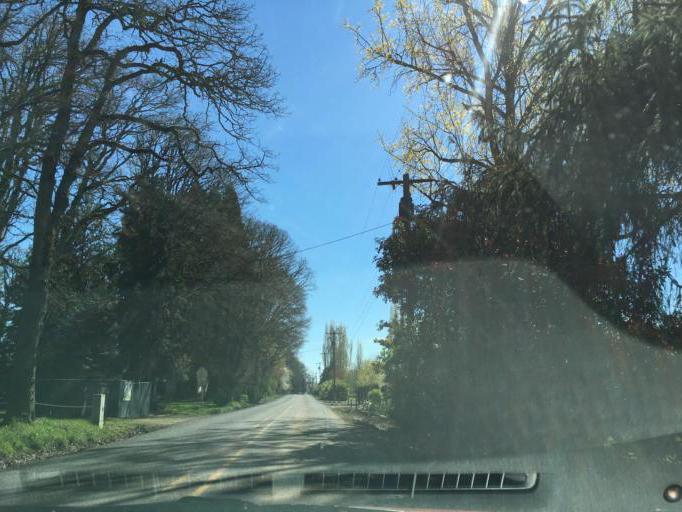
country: US
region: Oregon
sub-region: Marion County
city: Hubbard
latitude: 45.1353
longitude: -122.7569
